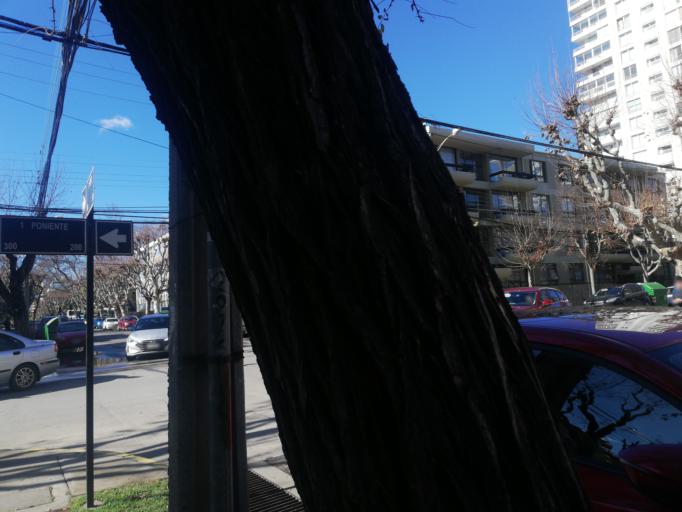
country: CL
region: Valparaiso
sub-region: Provincia de Valparaiso
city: Vina del Mar
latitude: -33.0203
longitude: -71.5526
